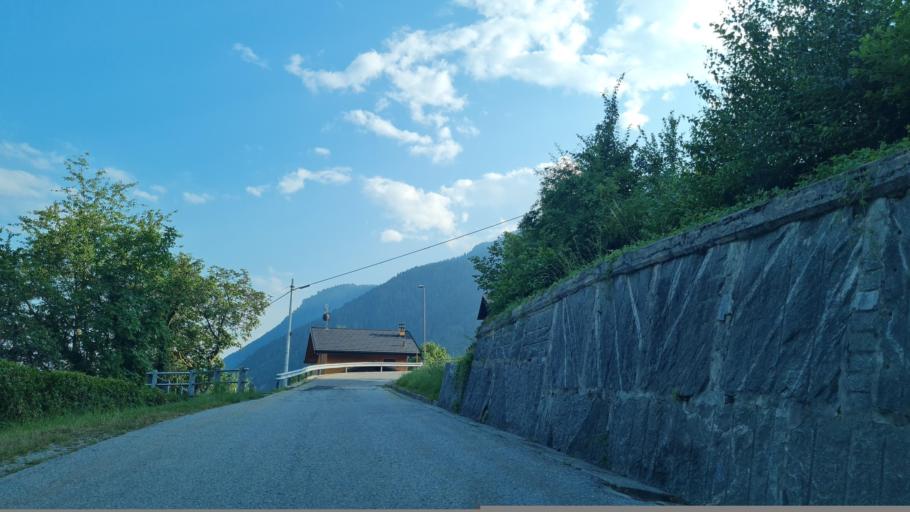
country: IT
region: Piedmont
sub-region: Provincia Verbano-Cusio-Ossola
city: Crodo
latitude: 46.2276
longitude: 8.3106
